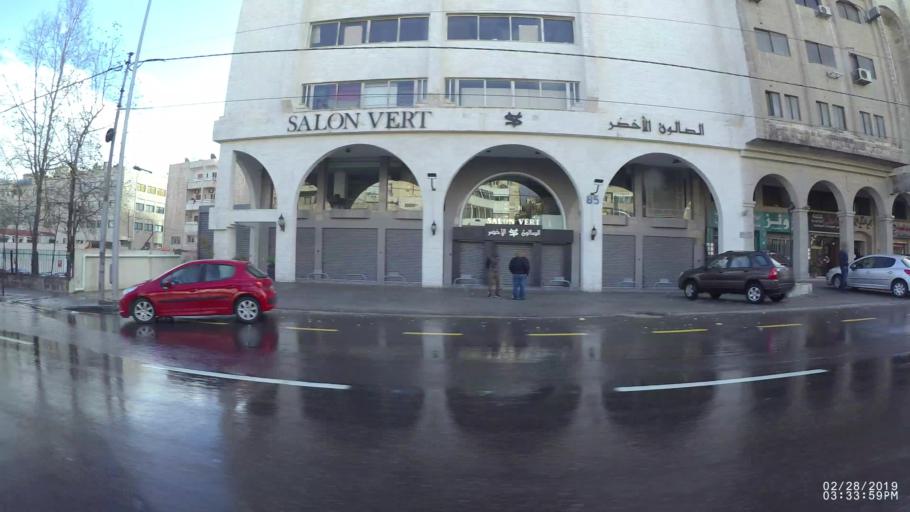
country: JO
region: Amman
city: Al Jubayhah
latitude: 31.9941
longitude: 35.8877
